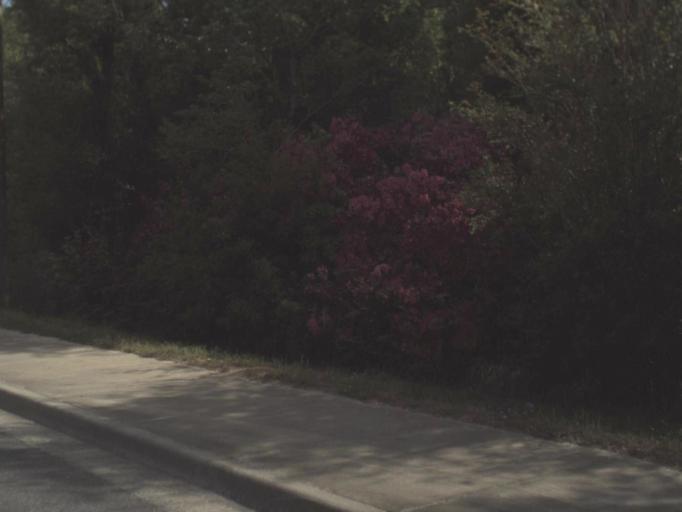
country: US
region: Florida
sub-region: Santa Rosa County
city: East Milton
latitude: 30.6152
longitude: -86.9606
